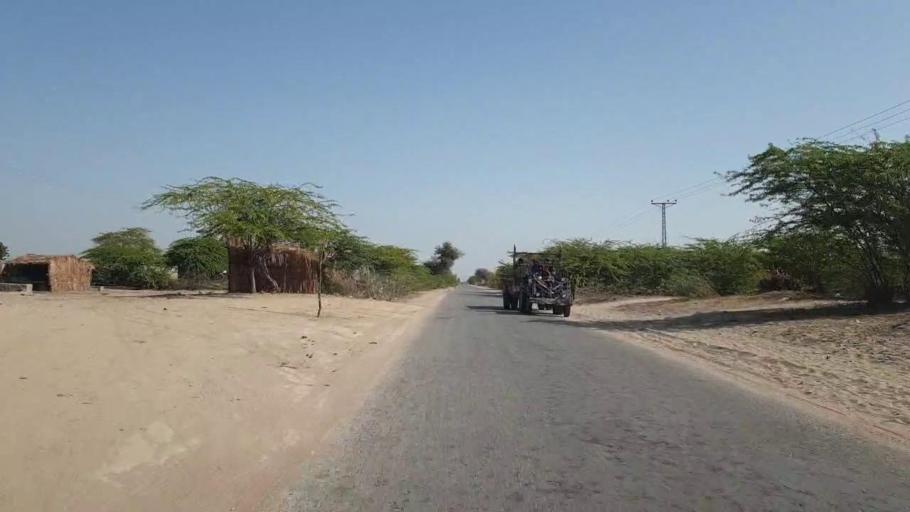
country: PK
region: Sindh
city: Chor
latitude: 25.4526
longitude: 69.7577
